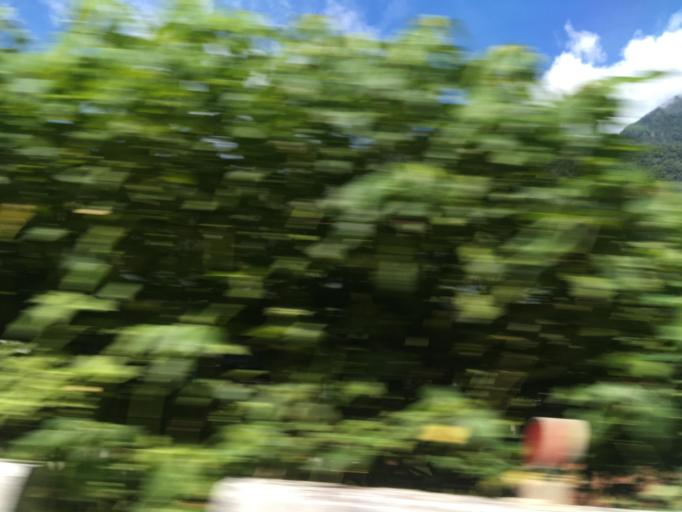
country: TW
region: Taiwan
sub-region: Yilan
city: Yilan
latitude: 24.4356
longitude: 121.7503
